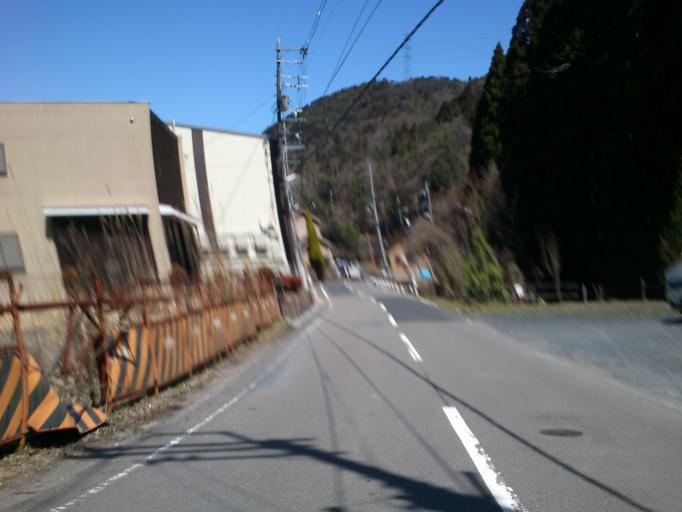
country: JP
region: Kyoto
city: Uji
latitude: 34.9275
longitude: 135.8552
